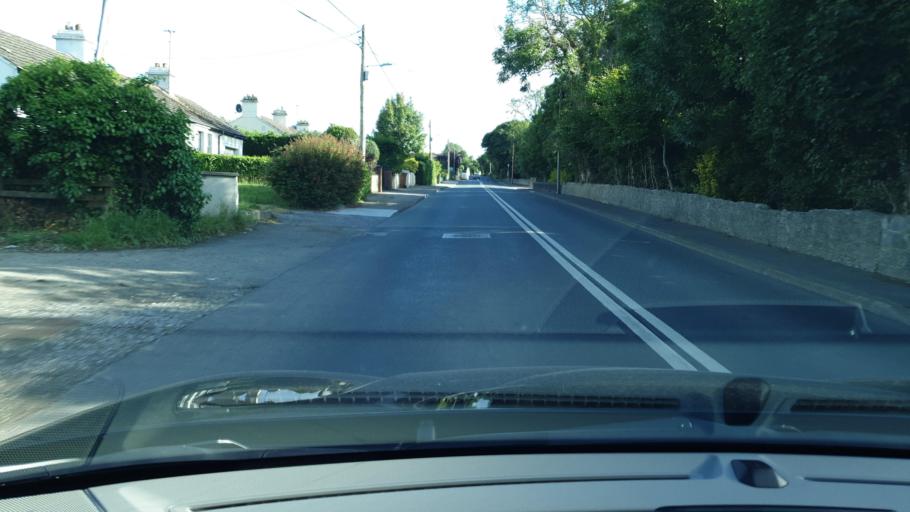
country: IE
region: Leinster
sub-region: Fingal County
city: Skerries
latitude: 53.5637
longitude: -6.1031
